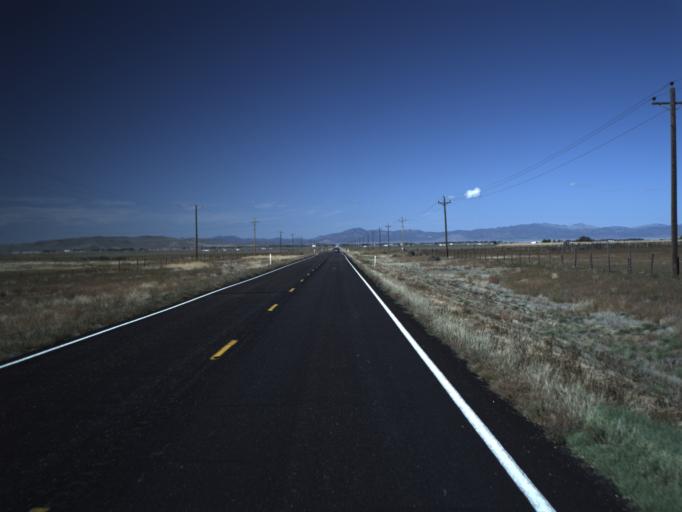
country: US
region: Utah
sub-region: Washington County
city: Enterprise
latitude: 37.6838
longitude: -113.5848
